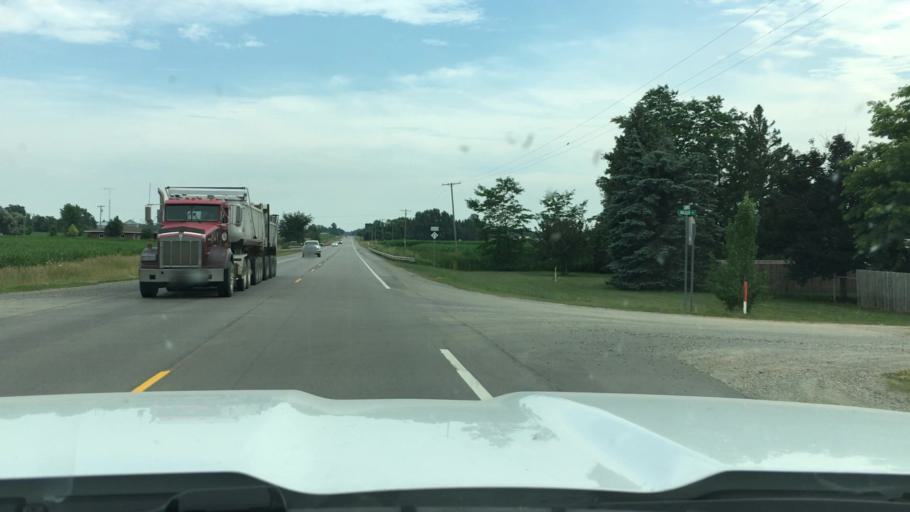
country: US
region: Michigan
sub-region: Sanilac County
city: Marlette
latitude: 43.3715
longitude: -83.0856
